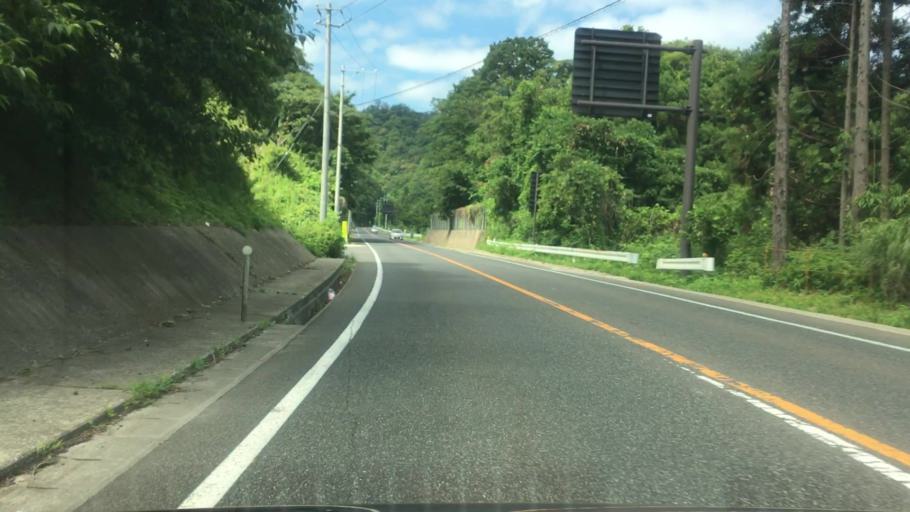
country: JP
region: Tottori
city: Tottori
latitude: 35.5979
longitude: 134.3660
